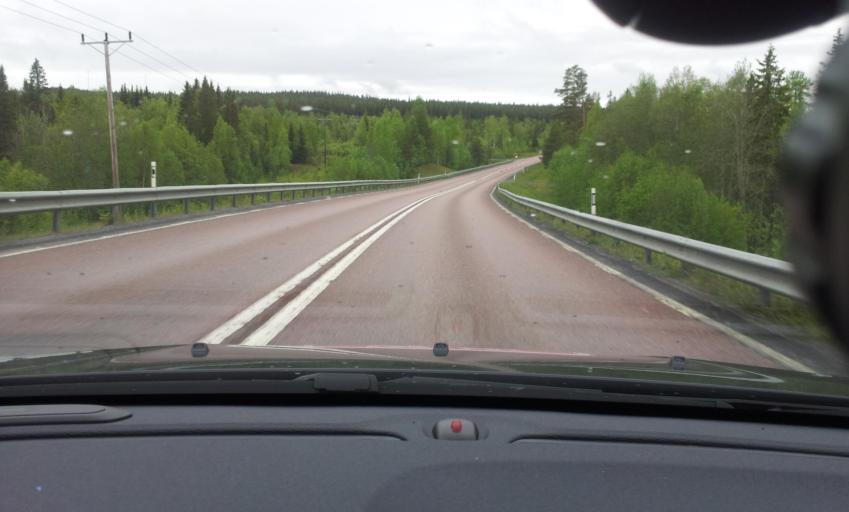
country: SE
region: Jaemtland
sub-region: Krokoms Kommun
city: Valla
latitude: 63.3314
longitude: 13.9734
